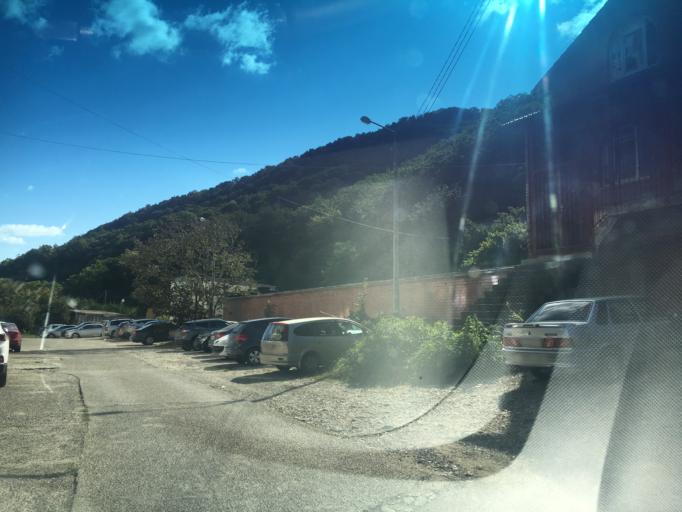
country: RU
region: Krasnodarskiy
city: Nebug
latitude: 44.1798
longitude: 38.9739
